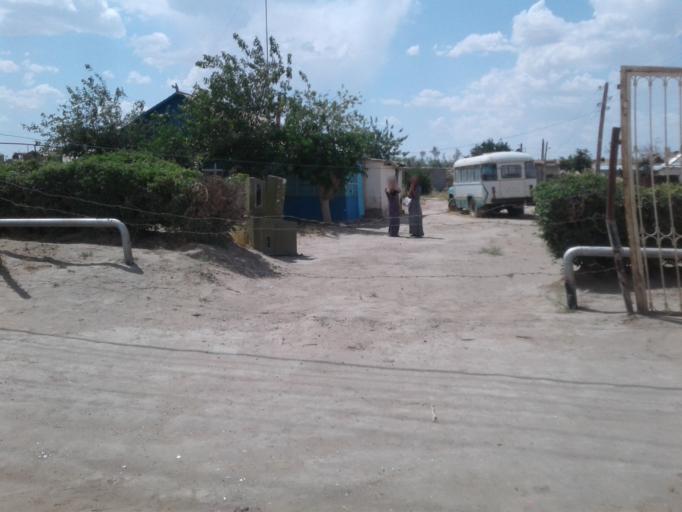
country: TM
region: Ahal
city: Abadan
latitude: 38.7648
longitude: 58.4930
